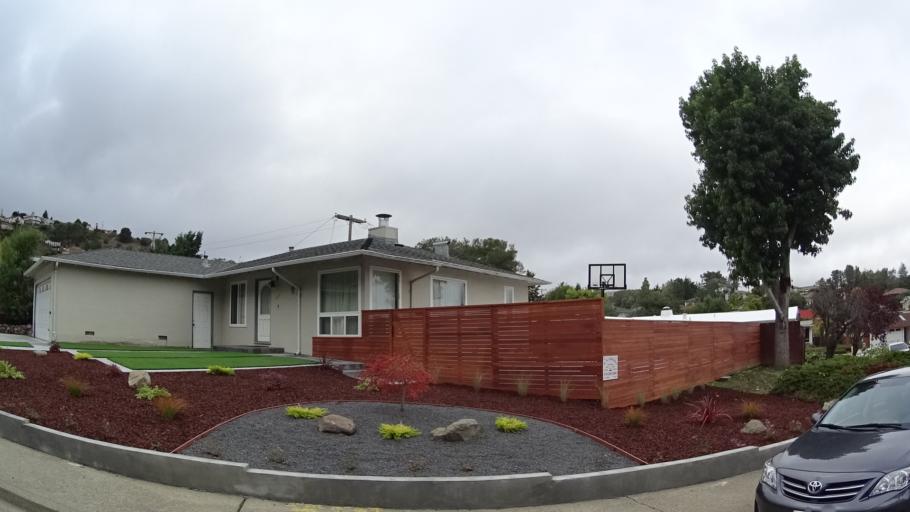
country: US
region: California
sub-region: San Mateo County
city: Millbrae
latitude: 37.5986
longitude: -122.4137
